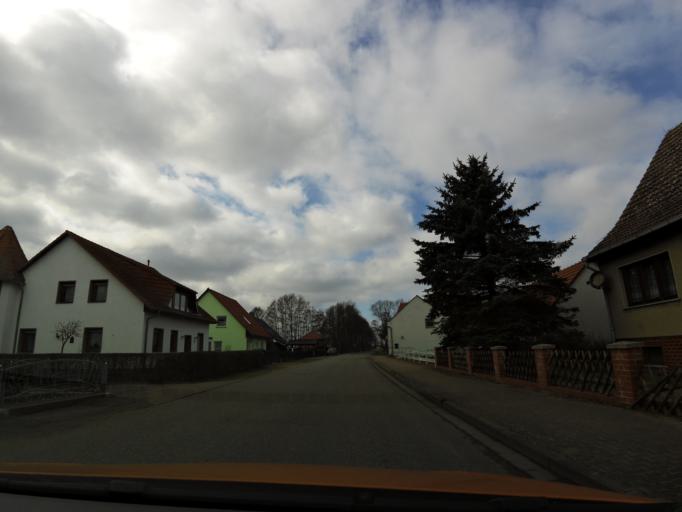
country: DE
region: Brandenburg
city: Rathenow
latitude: 52.6599
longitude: 12.3835
